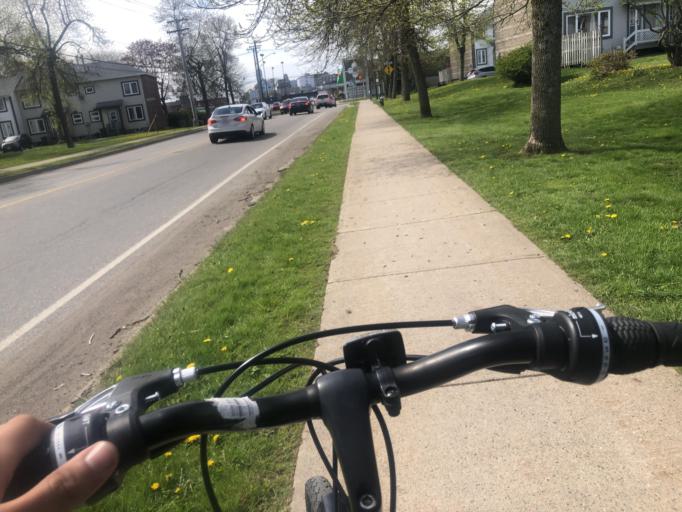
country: CA
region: New Brunswick
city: Saint John
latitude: 45.2809
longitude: -66.0781
